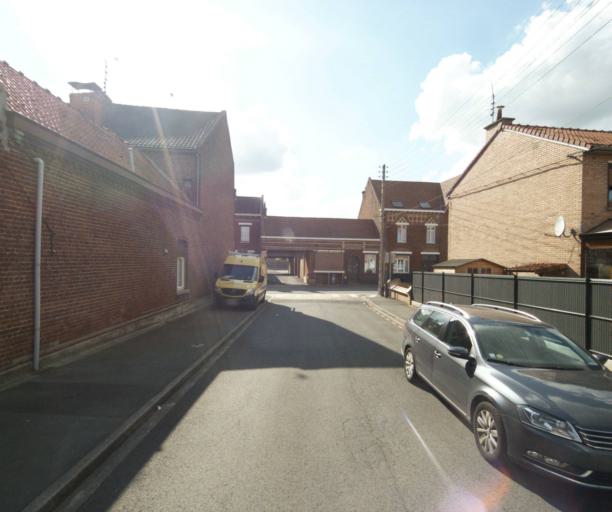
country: FR
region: Nord-Pas-de-Calais
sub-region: Departement du Nord
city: Sainghin-en-Weppes
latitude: 50.5668
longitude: 2.8945
